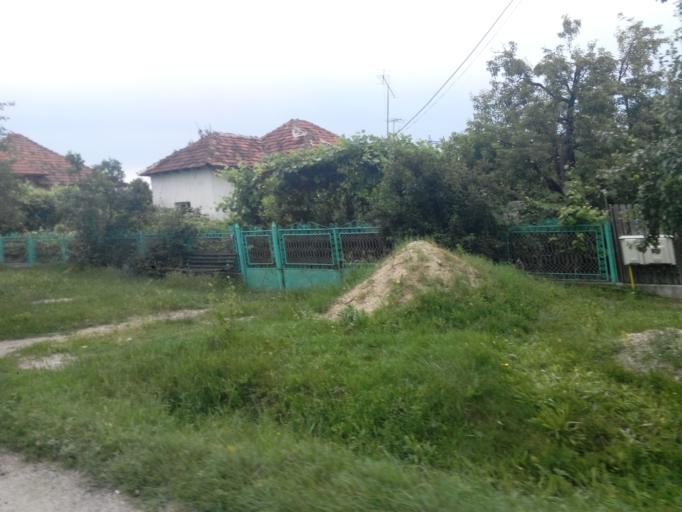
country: RO
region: Arges
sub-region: Comuna Bascov
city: Bascov
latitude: 44.9096
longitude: 24.8084
